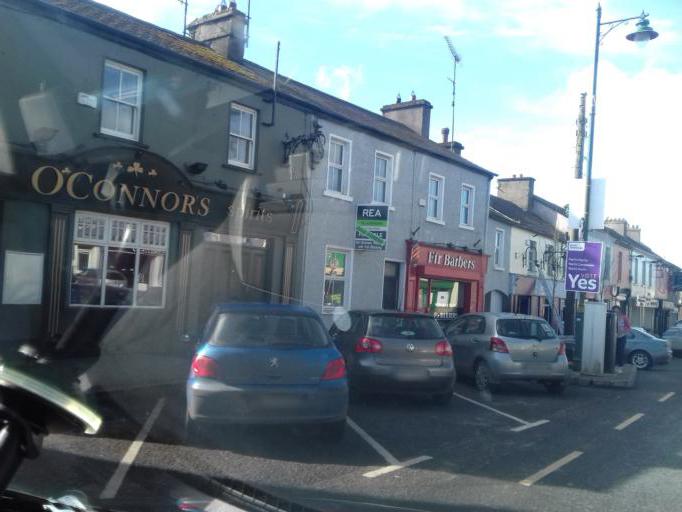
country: IE
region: Leinster
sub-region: An Mhi
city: Kells
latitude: 53.7264
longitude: -6.8779
